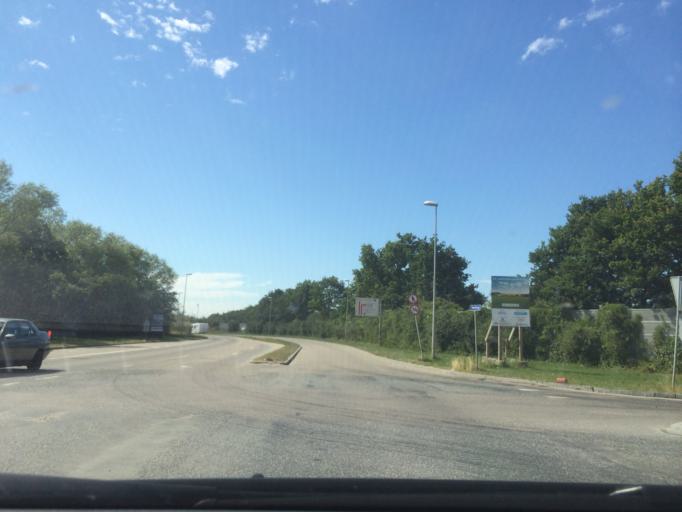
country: DK
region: Zealand
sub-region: Koge Kommune
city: Koge
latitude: 55.4701
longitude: 12.1884
